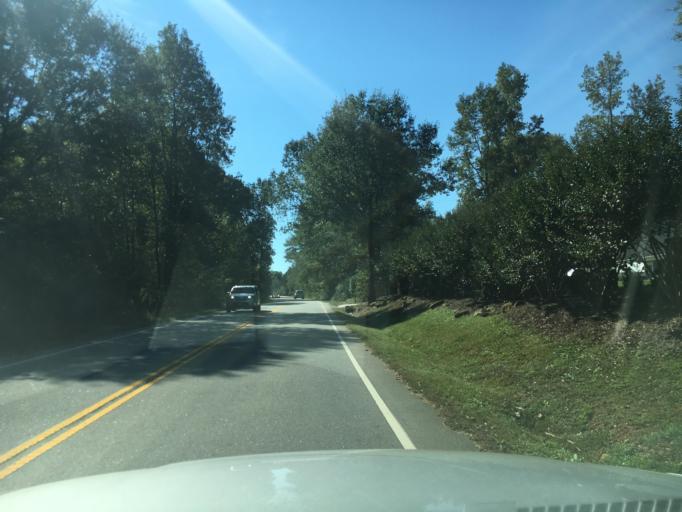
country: US
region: South Carolina
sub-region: Greenville County
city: Taylors
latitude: 34.8811
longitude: -82.2830
